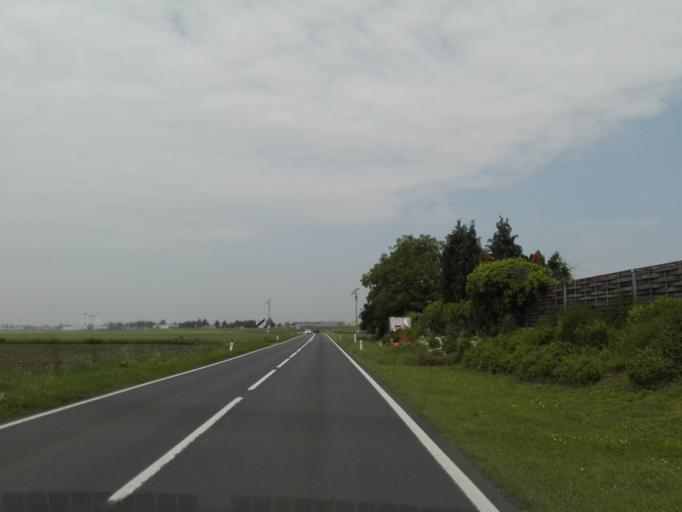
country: AT
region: Upper Austria
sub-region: Politischer Bezirk Urfahr-Umgebung
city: Goldworth
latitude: 48.2878
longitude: 14.1385
